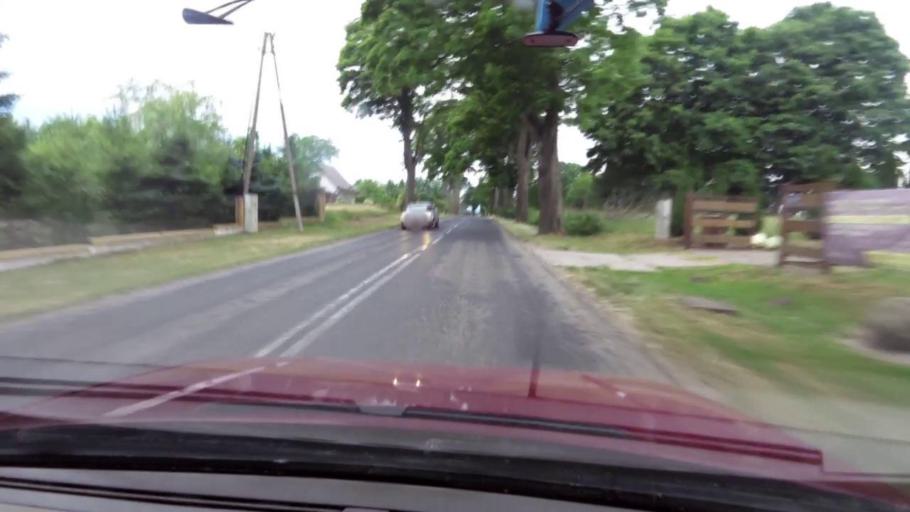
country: PL
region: West Pomeranian Voivodeship
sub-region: Powiat koszalinski
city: Sianow
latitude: 54.1710
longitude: 16.4076
